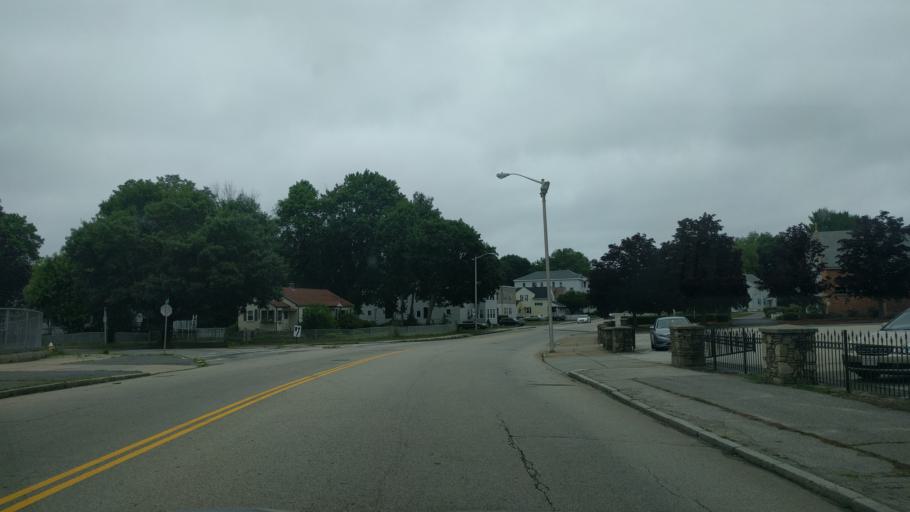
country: US
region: Massachusetts
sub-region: Worcester County
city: Sunderland
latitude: 42.2484
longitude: -71.7773
